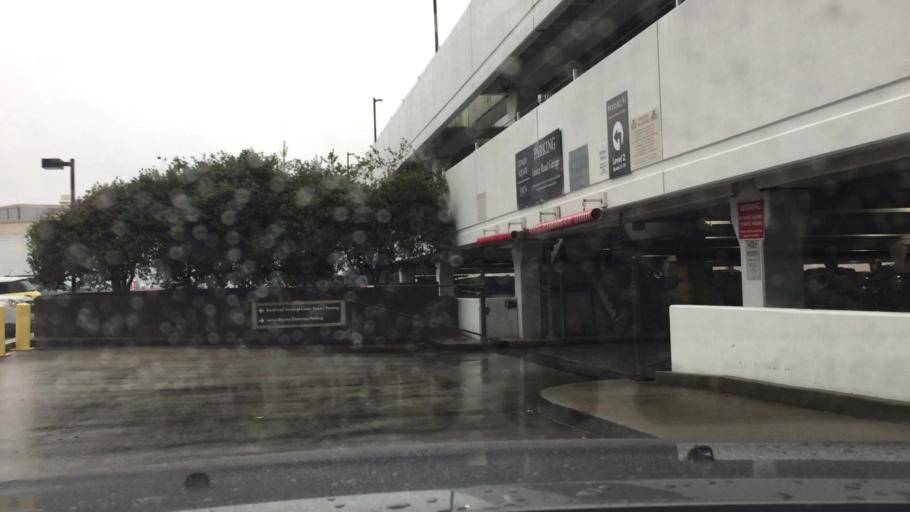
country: US
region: Georgia
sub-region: DeKalb County
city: North Atlanta
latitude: 33.8462
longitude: -84.3602
